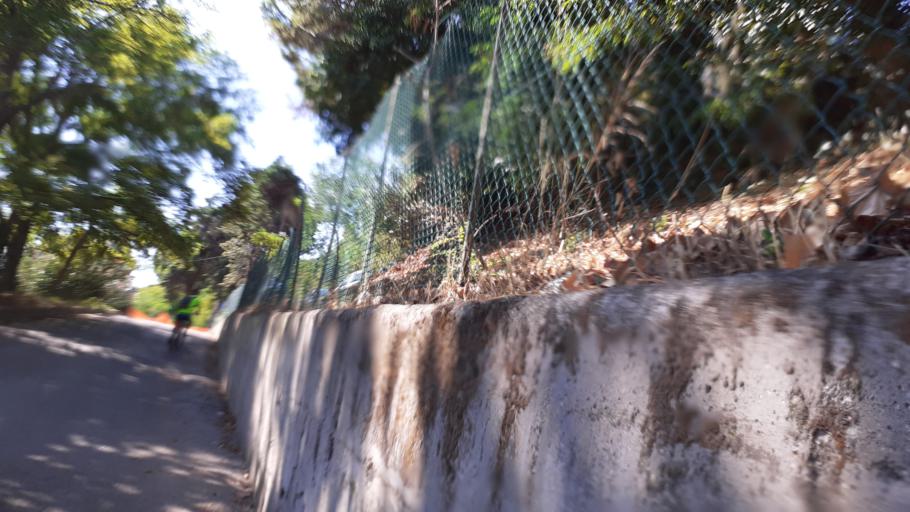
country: IT
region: Abruzzo
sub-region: Provincia di Chieti
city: Marina di Vasto
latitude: 42.1032
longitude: 14.7174
